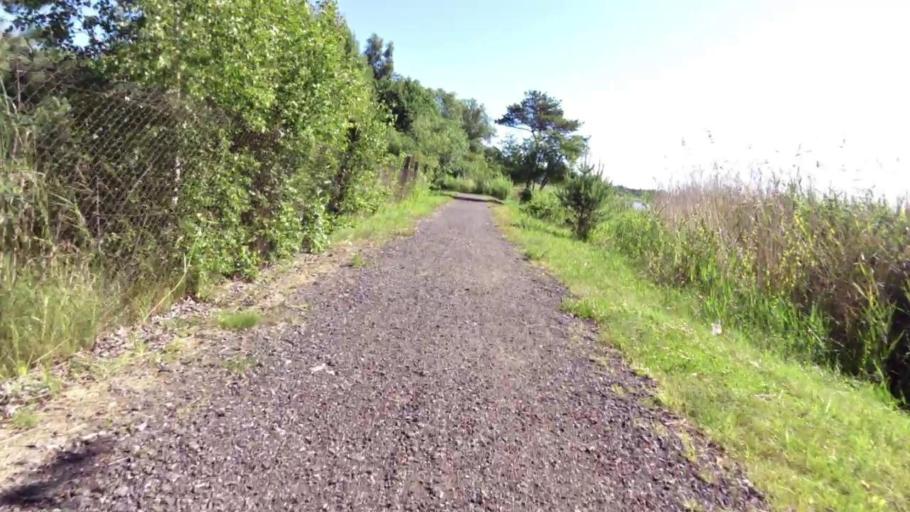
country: PL
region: West Pomeranian Voivodeship
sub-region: Powiat koszalinski
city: Mielno
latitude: 54.2775
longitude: 16.1216
